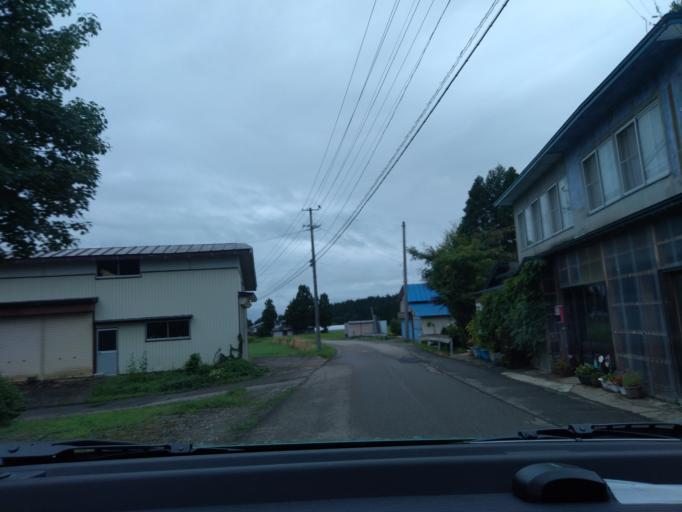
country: JP
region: Akita
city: Yokotemachi
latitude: 39.4228
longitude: 140.5990
